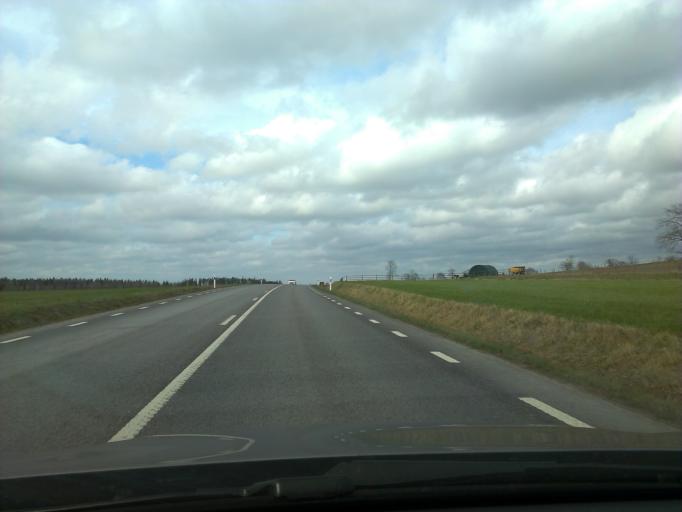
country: SE
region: Kronoberg
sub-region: Vaxjo Kommun
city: Gemla
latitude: 56.8449
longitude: 14.7139
